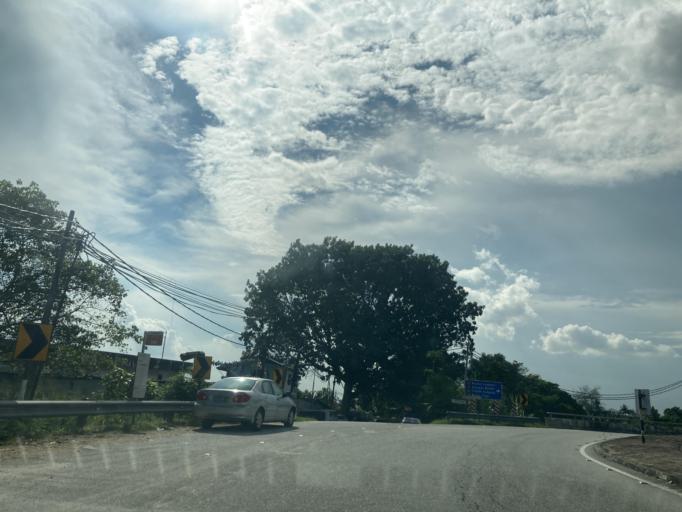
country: MY
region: Selangor
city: Kampung Baru Subang
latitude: 3.1460
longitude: 101.5437
